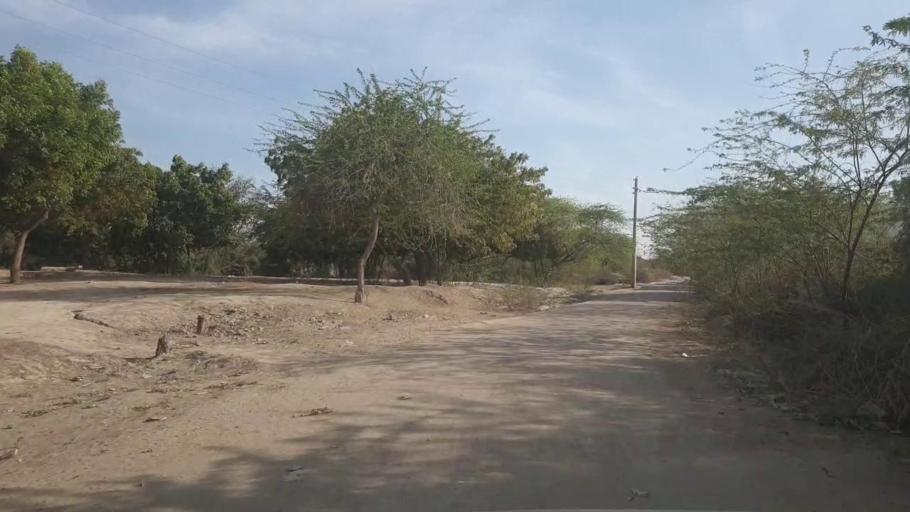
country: PK
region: Sindh
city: Nabisar
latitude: 25.0669
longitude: 69.6395
